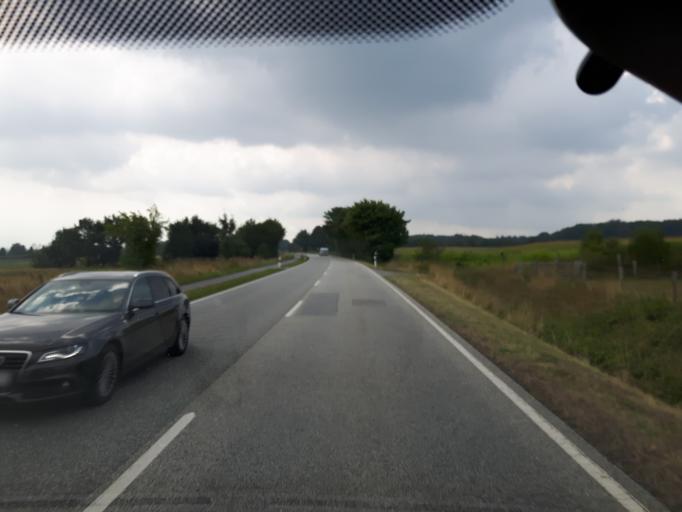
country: DE
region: Schleswig-Holstein
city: Holzbunge
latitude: 54.3700
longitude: 9.7025
